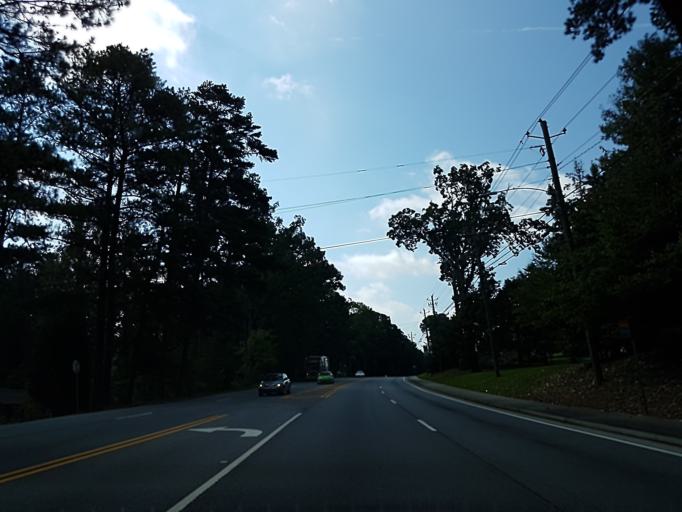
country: US
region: Georgia
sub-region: DeKalb County
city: North Druid Hills
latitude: 33.8306
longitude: -84.3093
